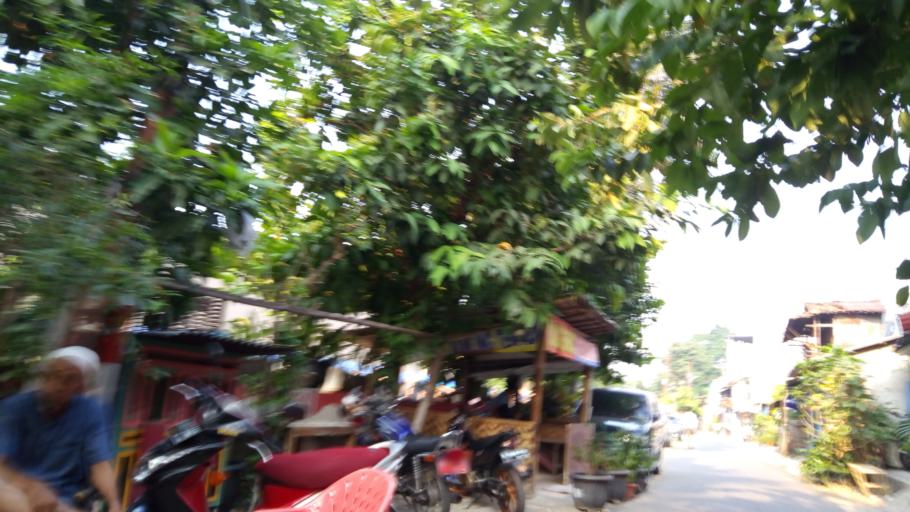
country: ID
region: Jakarta Raya
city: Jakarta
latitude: -6.1959
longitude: 106.8557
